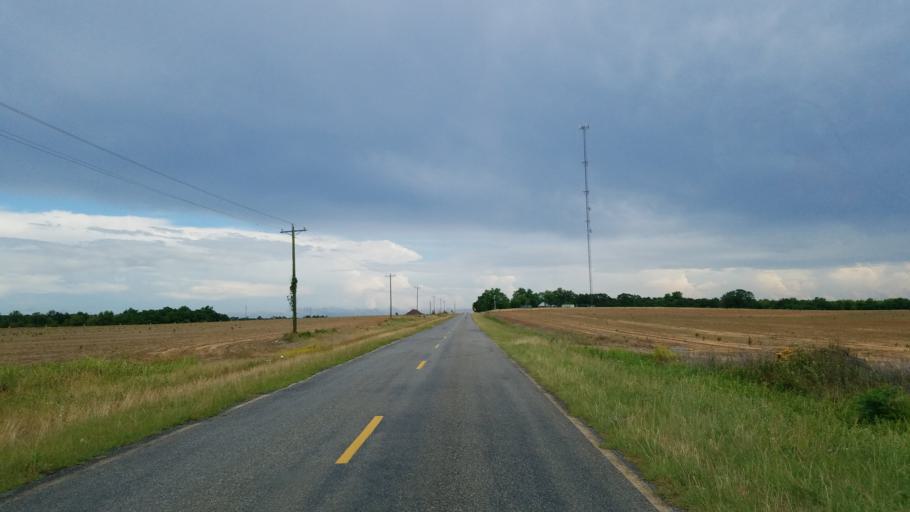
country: US
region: Georgia
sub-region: Dooly County
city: Vienna
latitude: 32.1583
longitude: -83.7982
